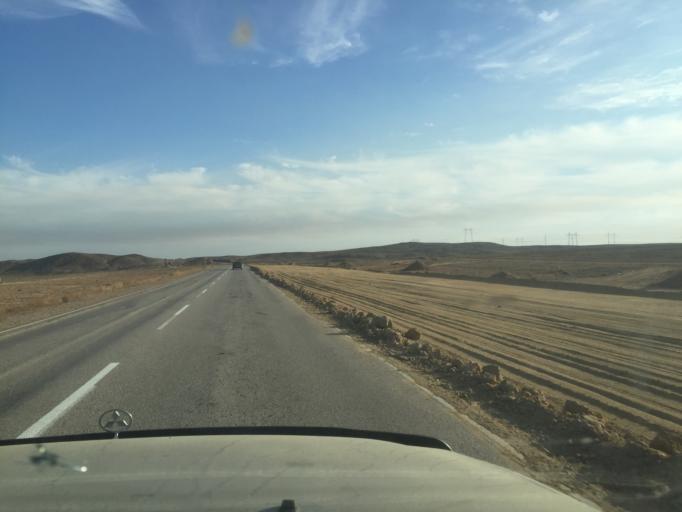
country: KZ
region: Zhambyl
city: Mynaral
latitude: 45.5161
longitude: 73.4929
